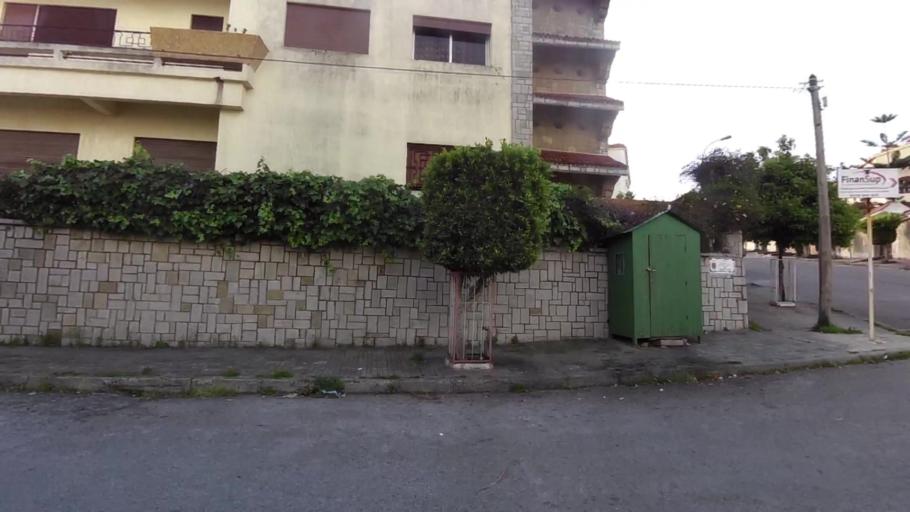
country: MA
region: Tanger-Tetouan
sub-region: Tanger-Assilah
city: Tangier
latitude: 35.7679
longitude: -5.7981
